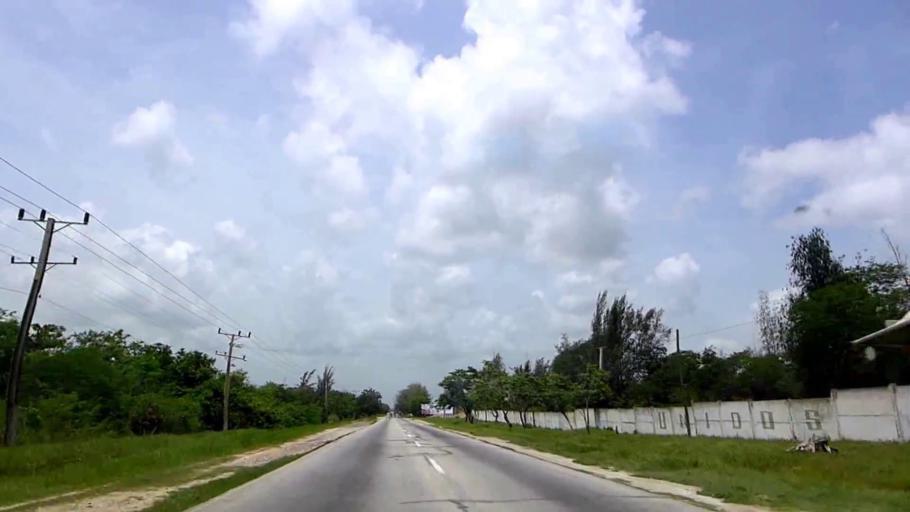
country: CU
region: Holguin
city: Cacocum
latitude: 20.7970
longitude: -76.2972
